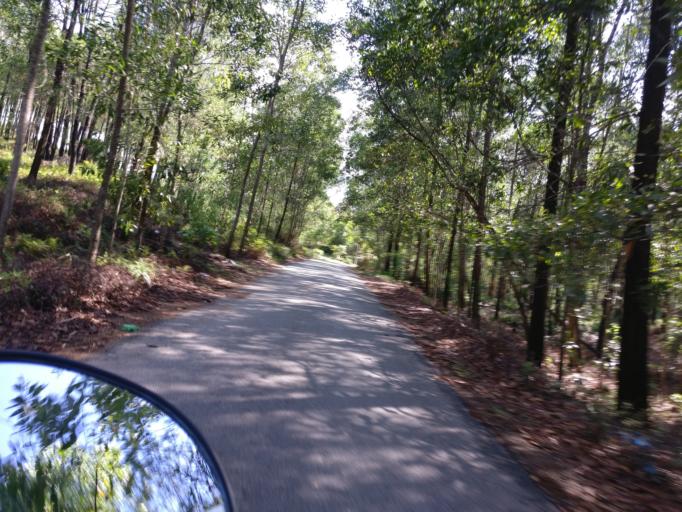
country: VN
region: Thua Thien-Hue
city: Hue
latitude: 16.4071
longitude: 107.5930
